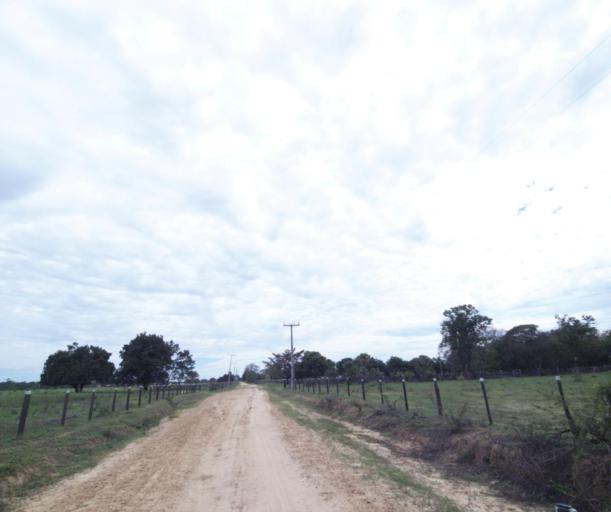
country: BR
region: Bahia
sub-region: Carinhanha
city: Carinhanha
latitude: -14.2520
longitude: -44.3537
